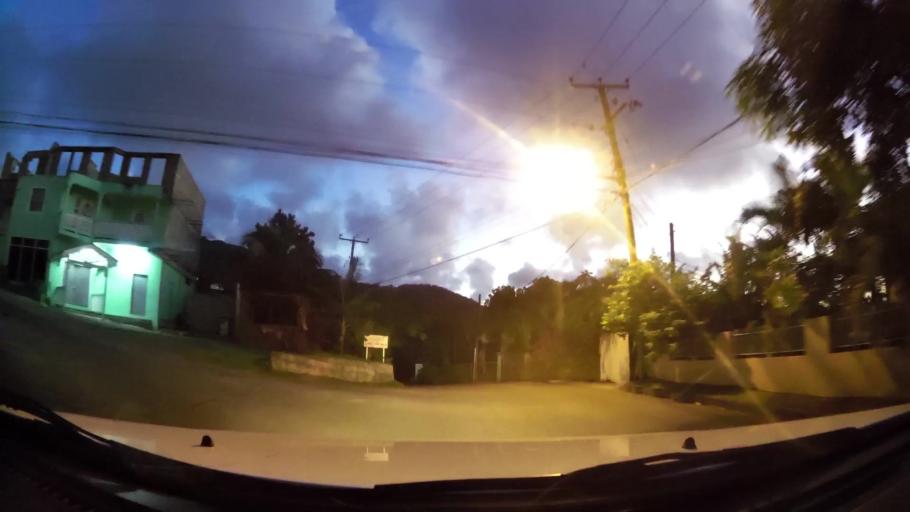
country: LC
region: Castries Quarter
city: Bisee
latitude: 14.0312
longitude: -60.9459
